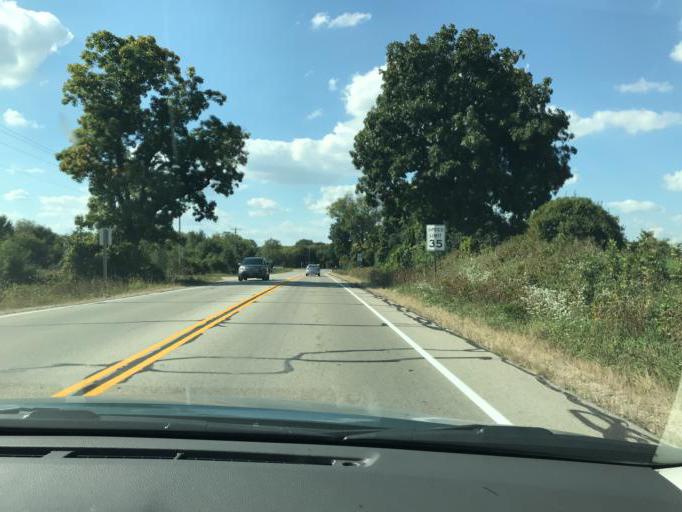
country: US
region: Wisconsin
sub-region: Walworth County
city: Williams Bay
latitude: 42.6165
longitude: -88.5773
